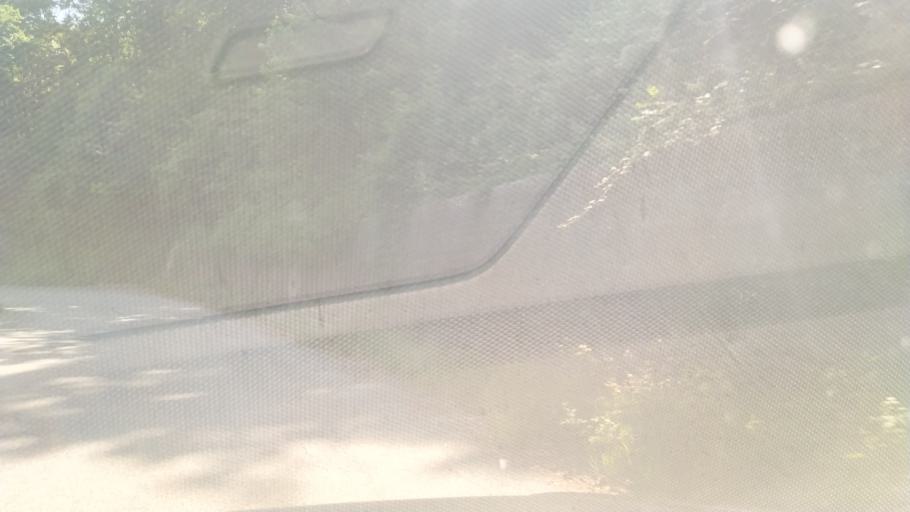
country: IT
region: Piedmont
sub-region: Provincia di Torino
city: Cintano
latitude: 45.4158
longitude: 7.7137
